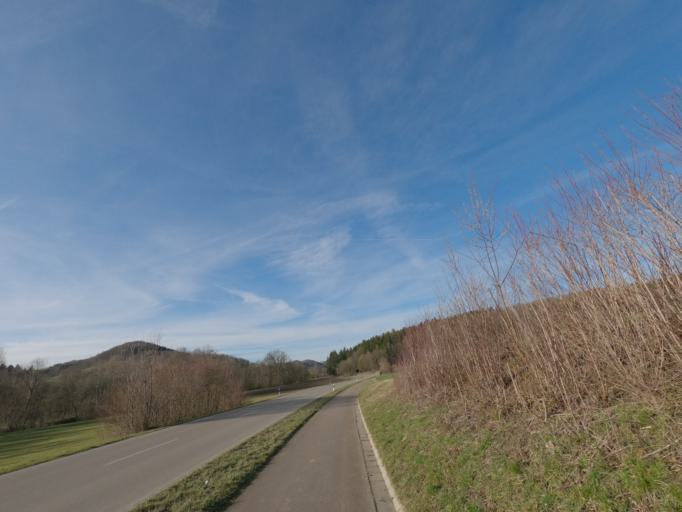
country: DE
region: Baden-Wuerttemberg
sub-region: Regierungsbezirk Stuttgart
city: Donzdorf
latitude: 48.6991
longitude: 9.8011
